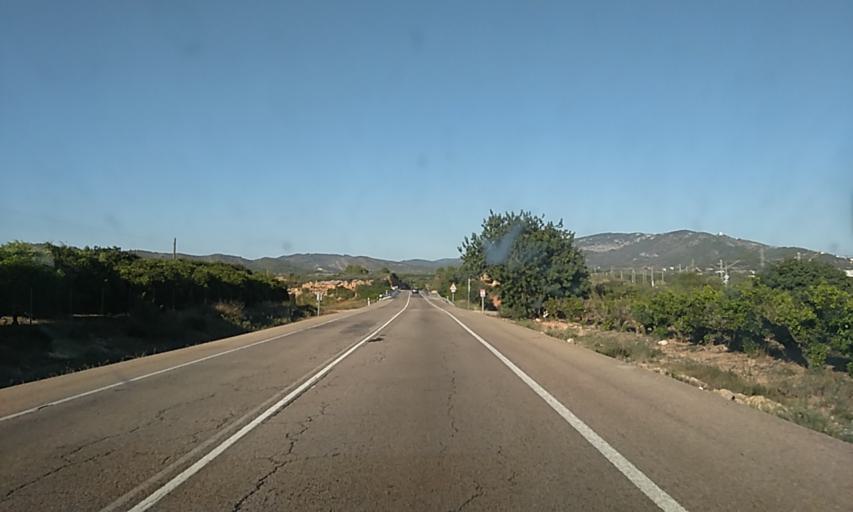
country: ES
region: Valencia
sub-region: Provincia de Castello
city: Torreblanca
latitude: 40.2356
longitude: 0.2227
